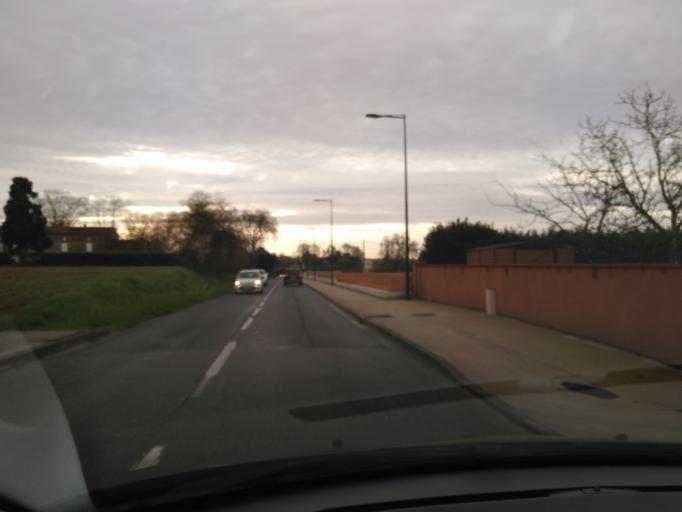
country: FR
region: Midi-Pyrenees
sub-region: Departement de la Haute-Garonne
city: Castelnau-d'Estretefonds
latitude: 43.7799
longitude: 1.3648
